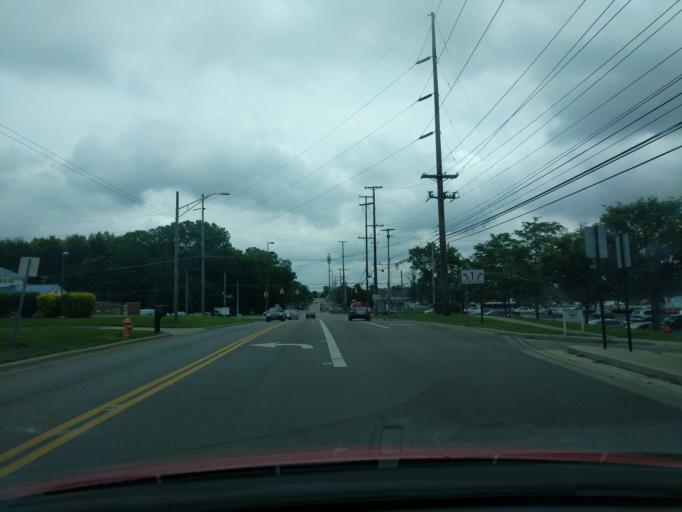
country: US
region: Ohio
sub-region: Franklin County
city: Gahanna
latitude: 40.0334
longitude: -82.9117
